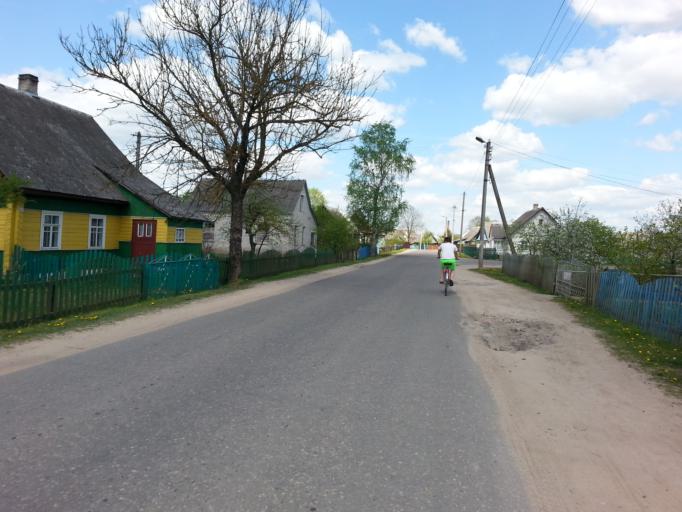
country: BY
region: Minsk
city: Narach
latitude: 54.9314
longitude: 26.6889
